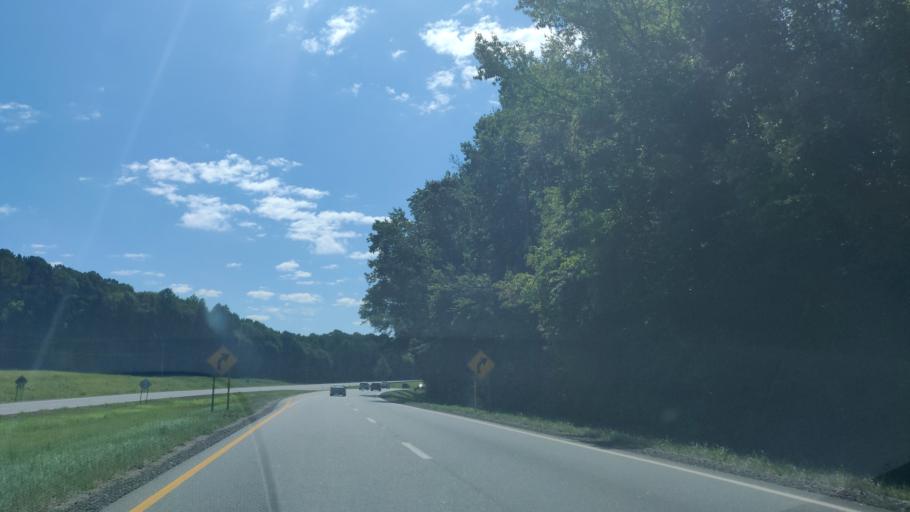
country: US
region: Alabama
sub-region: Lee County
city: Opelika
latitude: 32.6348
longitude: -85.2904
